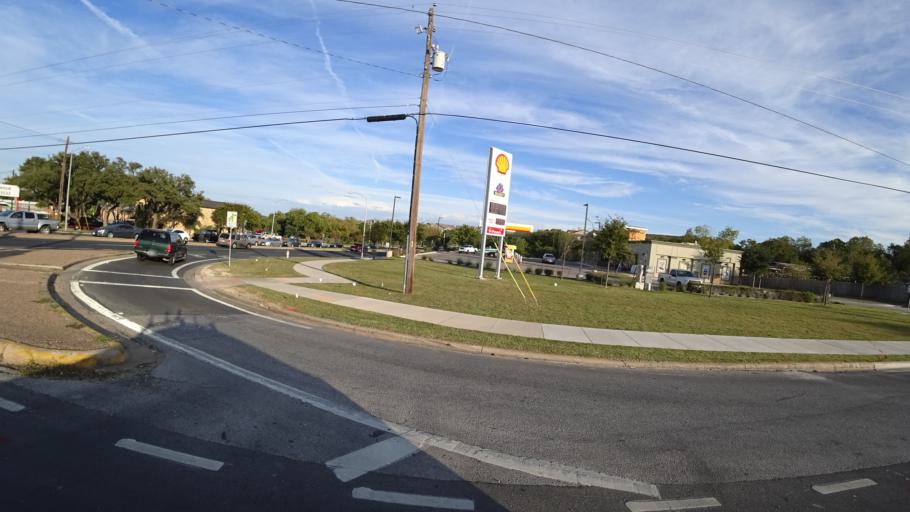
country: US
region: Texas
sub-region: Travis County
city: Onion Creek
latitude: 30.2046
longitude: -97.7748
